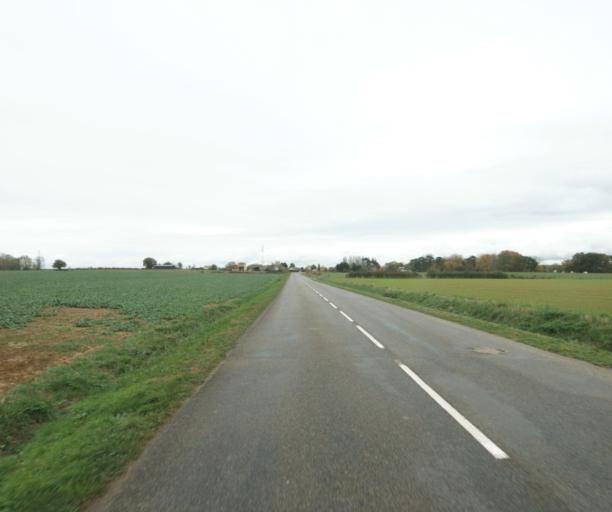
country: FR
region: Rhone-Alpes
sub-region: Departement de l'Ain
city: Pont-de-Vaux
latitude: 46.4653
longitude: 4.8663
